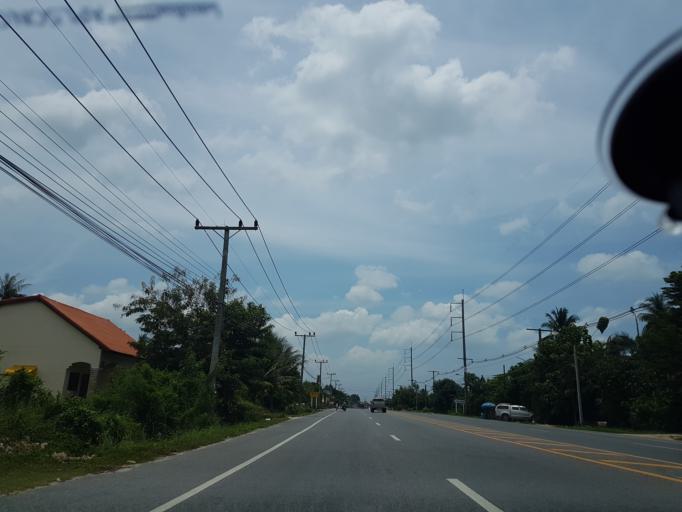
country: TH
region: Songkhla
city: Songkhla
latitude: 7.0997
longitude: 100.6336
